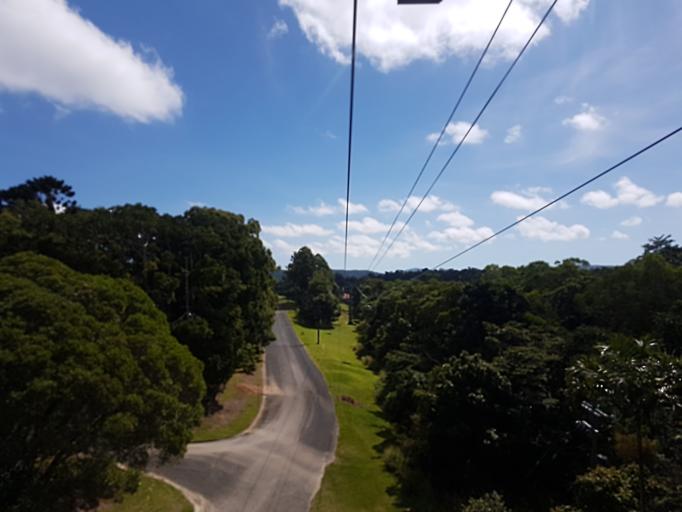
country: AU
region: Queensland
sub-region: Tablelands
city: Kuranda
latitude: -16.8230
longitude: 145.6408
